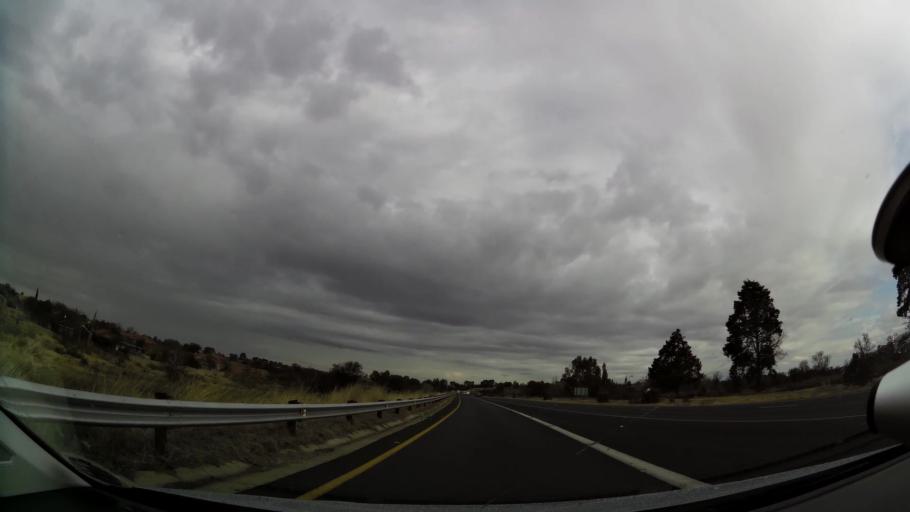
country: ZA
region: Orange Free State
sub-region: Fezile Dabi District Municipality
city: Kroonstad
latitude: -27.6593
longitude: 27.2512
